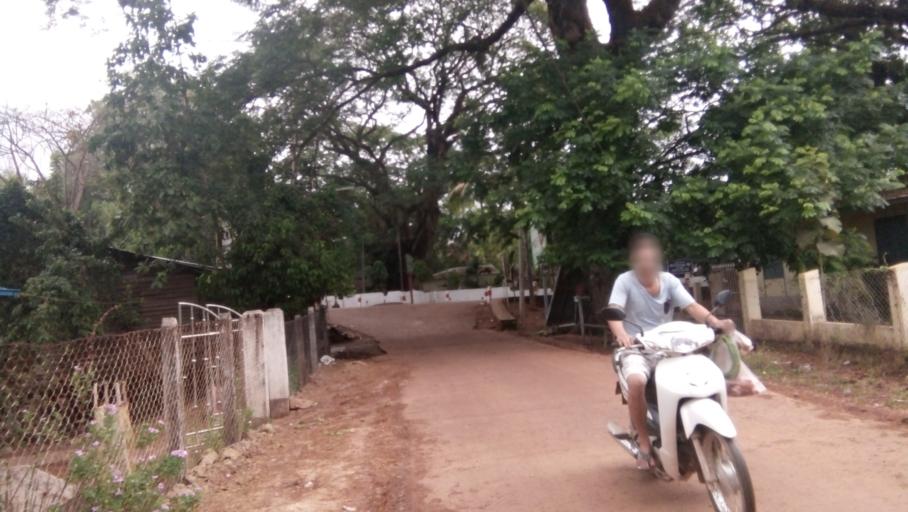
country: MM
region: Kayin
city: Hpa-an
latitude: 17.1203
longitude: 97.8177
